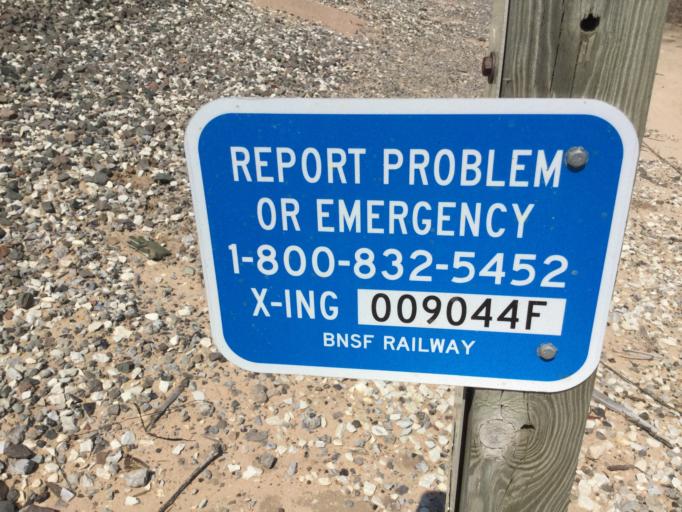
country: US
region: Kansas
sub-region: Pawnee County
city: Larned
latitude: 37.9489
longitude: -99.1507
